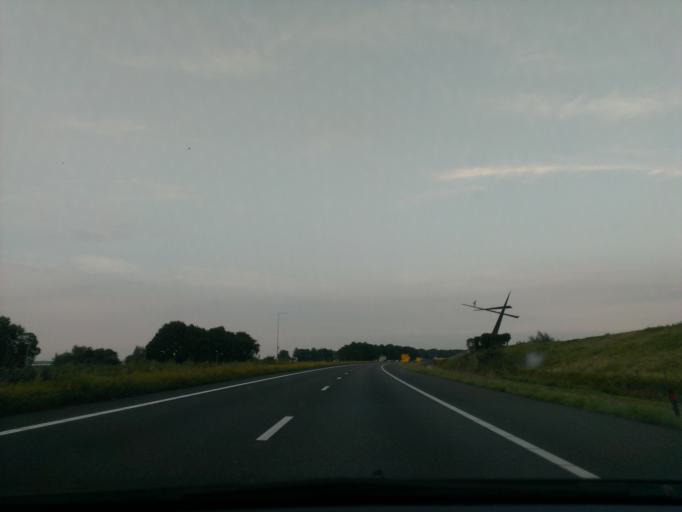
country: NL
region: Gelderland
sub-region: Gemeente Ermelo
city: Horst
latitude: 52.3269
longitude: 5.5794
